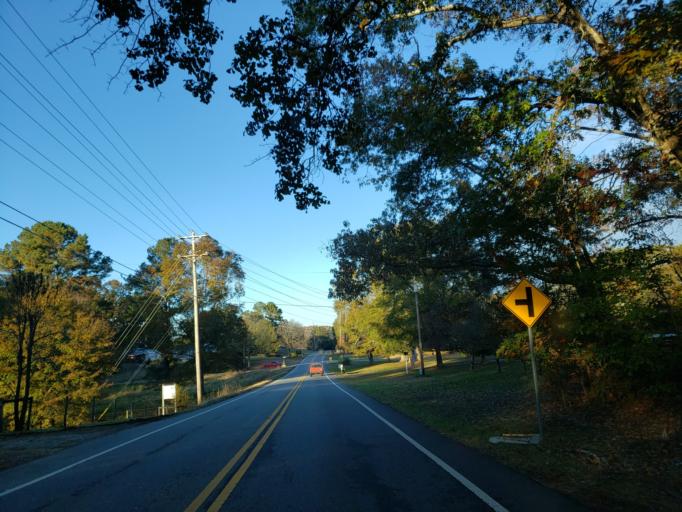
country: US
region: Georgia
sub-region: Cherokee County
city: Canton
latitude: 34.2199
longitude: -84.3799
